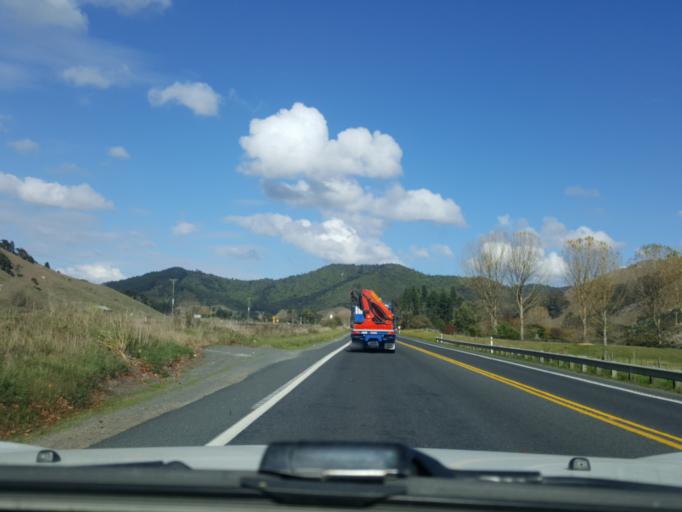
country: NZ
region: Waikato
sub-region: Waikato District
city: Ngaruawahia
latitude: -37.5864
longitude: 175.1596
